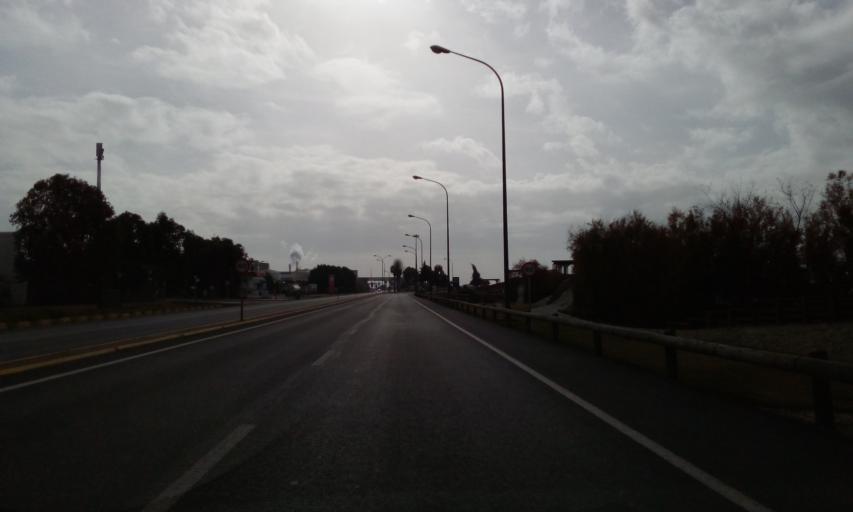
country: ES
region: Andalusia
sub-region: Provincia de Huelva
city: Huelva
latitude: 37.2353
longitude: -6.9536
